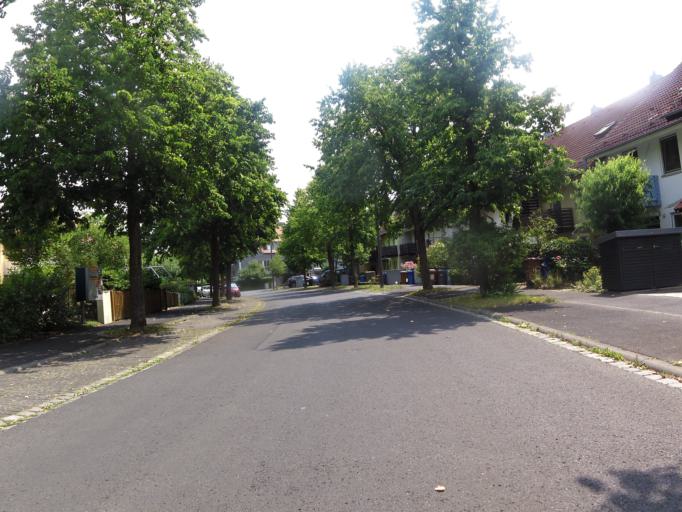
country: DE
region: Bavaria
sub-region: Regierungsbezirk Unterfranken
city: Randersacker
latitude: 49.7376
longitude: 9.9621
